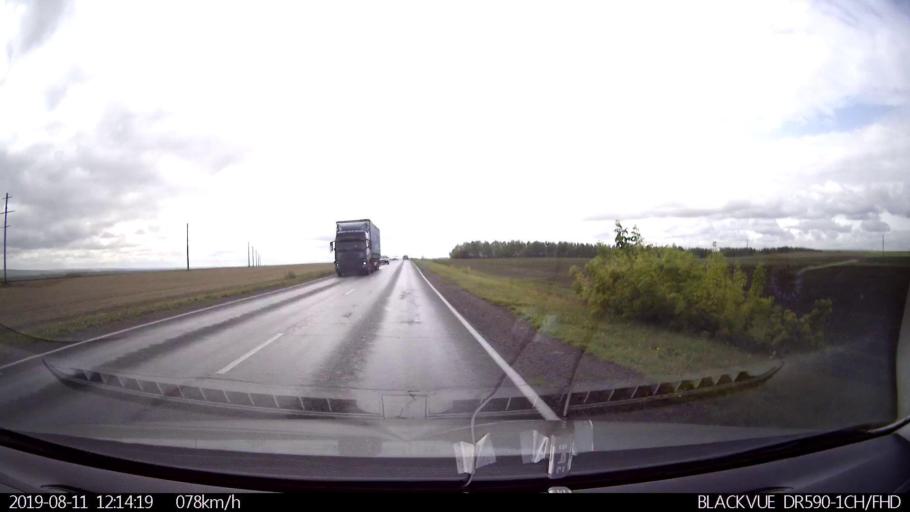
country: RU
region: Ulyanovsk
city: Ignatovka
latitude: 53.9533
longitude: 47.9815
